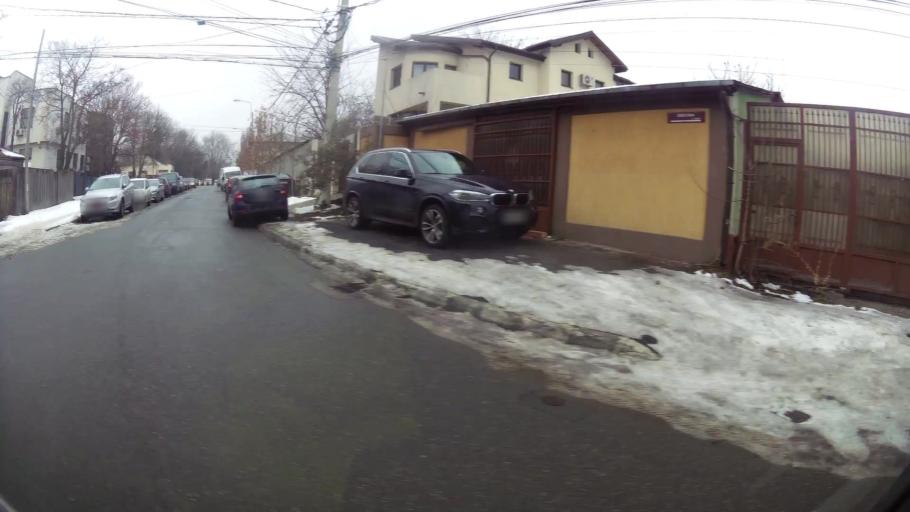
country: RO
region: Ilfov
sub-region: Comuna Popesti-Leordeni
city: Popesti-Leordeni
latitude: 44.4092
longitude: 26.1604
